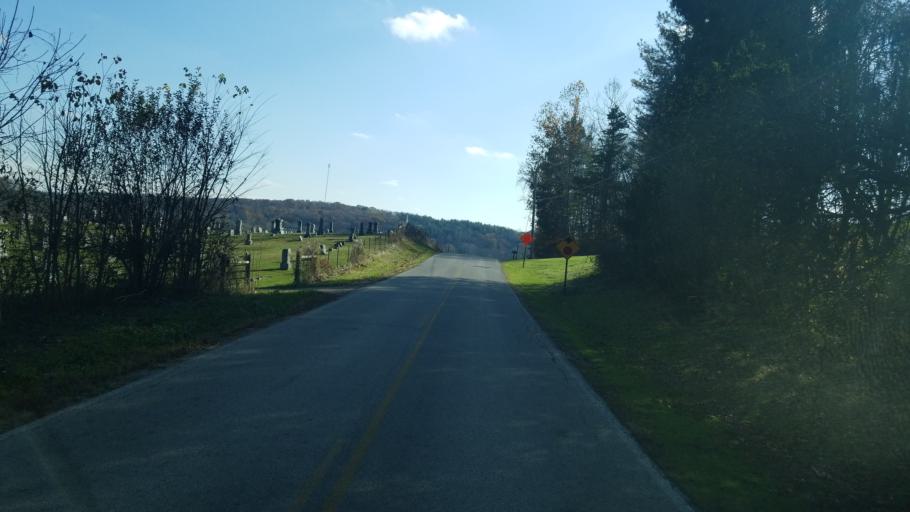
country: US
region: Ohio
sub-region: Sandusky County
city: Bellville
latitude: 40.6072
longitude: -82.4458
